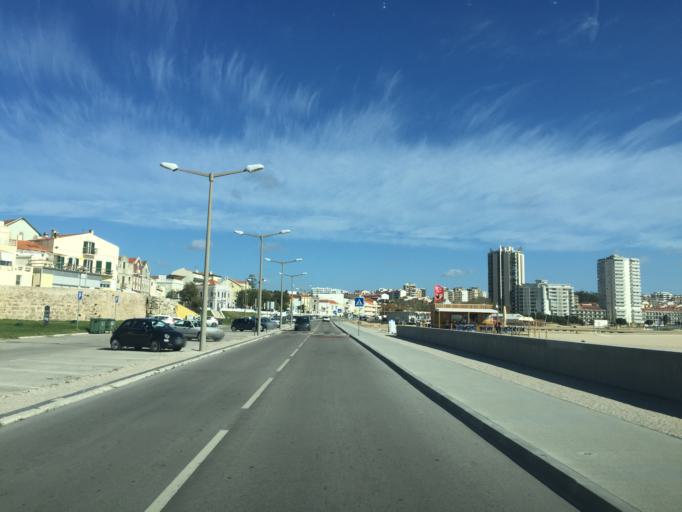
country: PT
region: Coimbra
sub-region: Figueira da Foz
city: Buarcos
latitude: 40.1641
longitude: -8.8787
